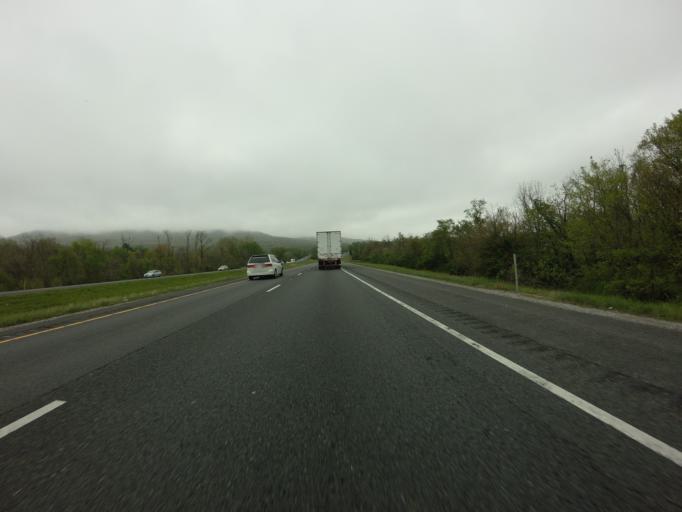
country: US
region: Maryland
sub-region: Washington County
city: Robinwood
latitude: 39.5765
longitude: -77.6271
